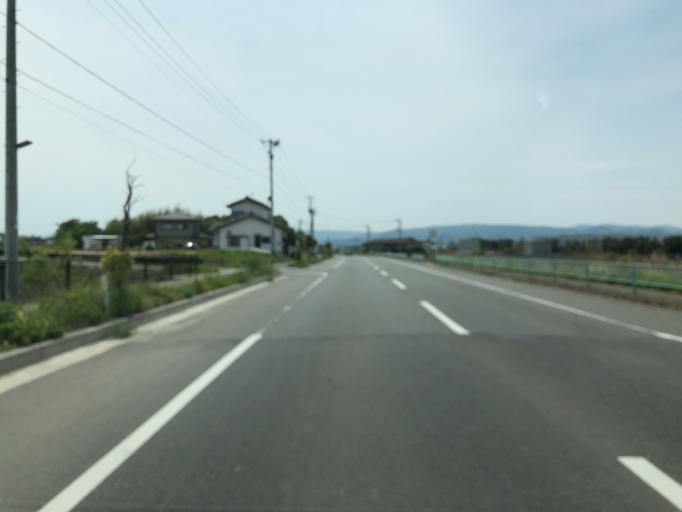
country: JP
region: Miyagi
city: Marumori
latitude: 37.8287
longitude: 140.9539
